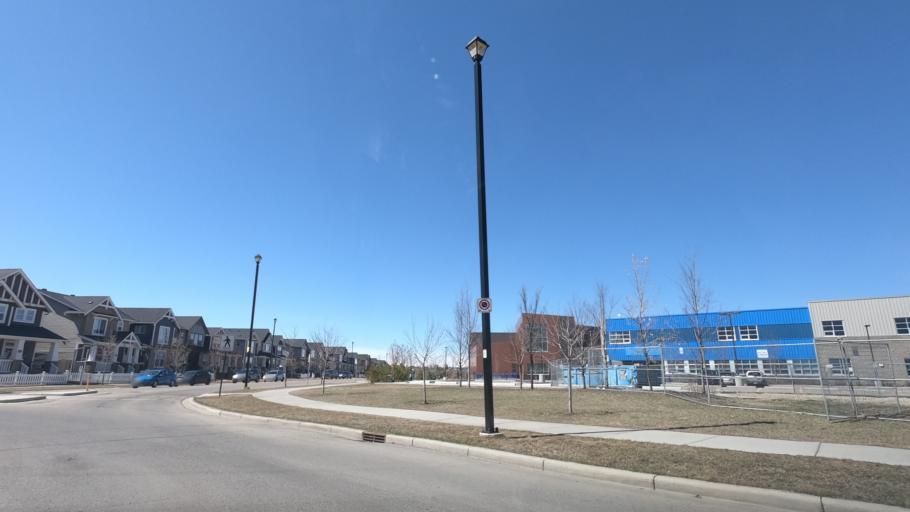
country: CA
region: Alberta
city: Airdrie
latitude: 51.3032
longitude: -114.0339
